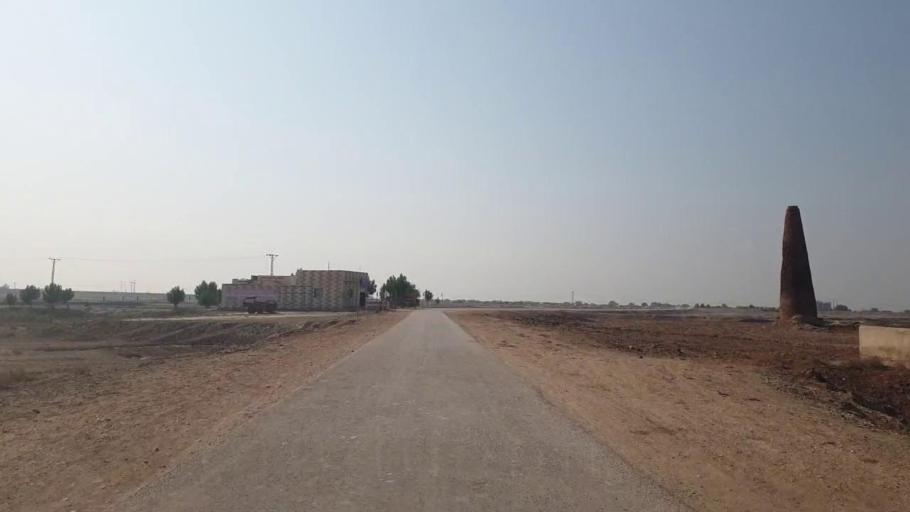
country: PK
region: Sindh
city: Sehwan
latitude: 26.4334
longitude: 67.8442
